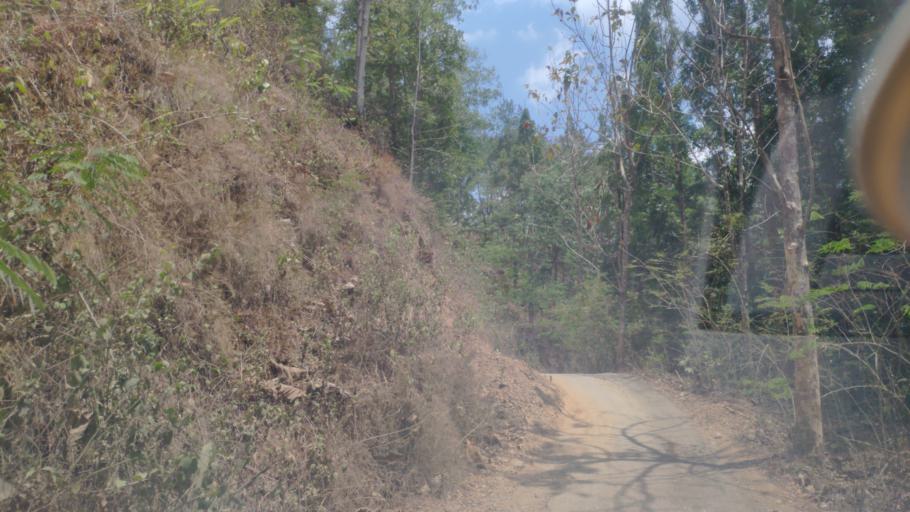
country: ID
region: Central Java
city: Gombong
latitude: -7.4800
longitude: 109.6128
